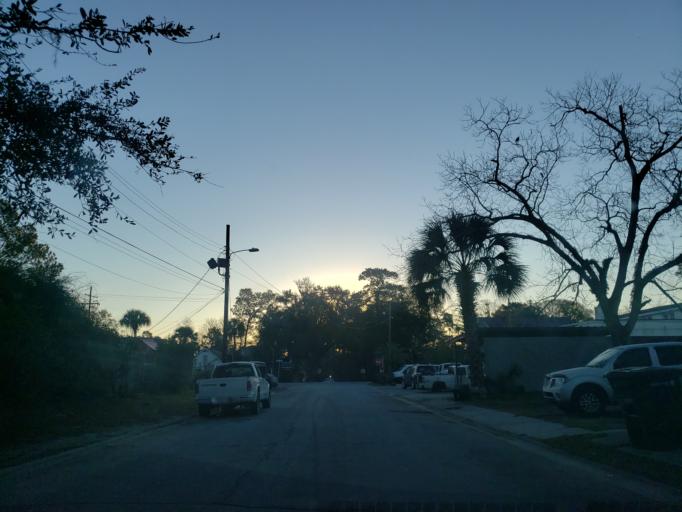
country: US
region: Georgia
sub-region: Chatham County
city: Savannah
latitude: 32.0403
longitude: -81.1077
